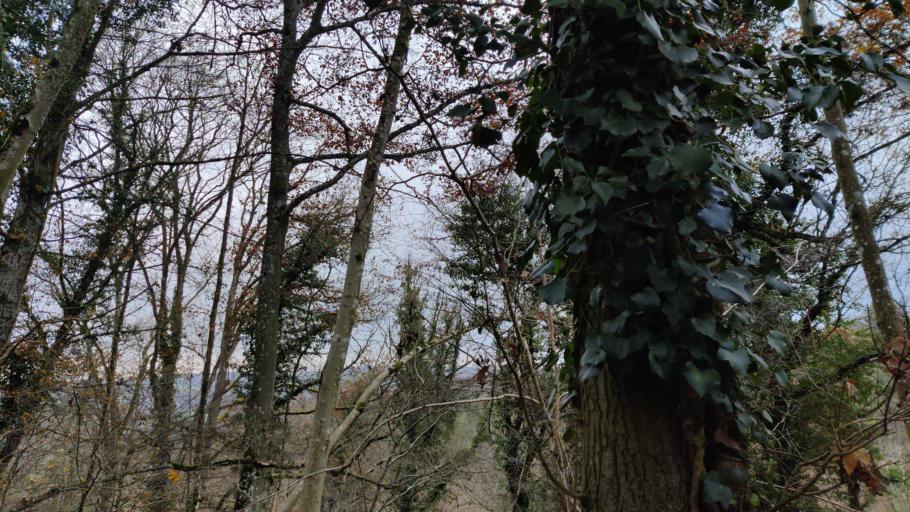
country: BE
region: Wallonia
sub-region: Province de Namur
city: Couvin
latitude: 50.0889
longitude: 4.6028
